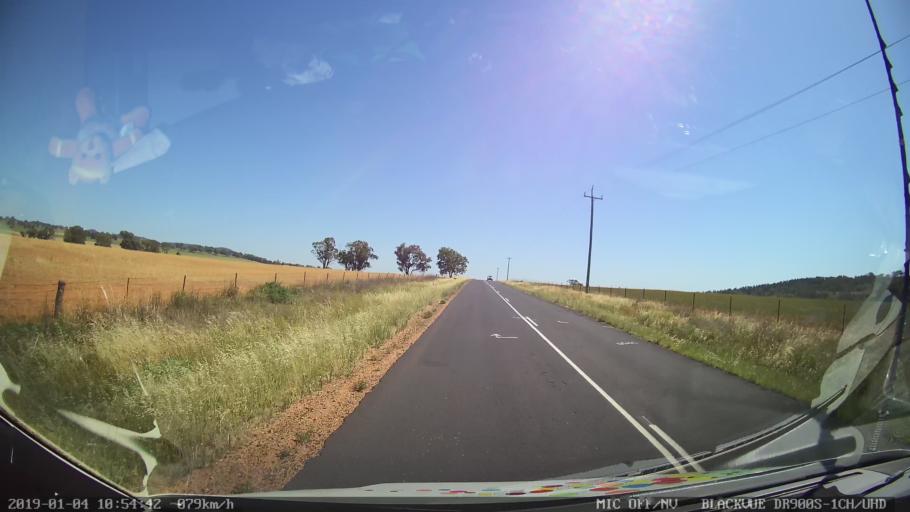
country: AU
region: New South Wales
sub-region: Cabonne
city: Molong
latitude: -33.2019
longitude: 148.6904
